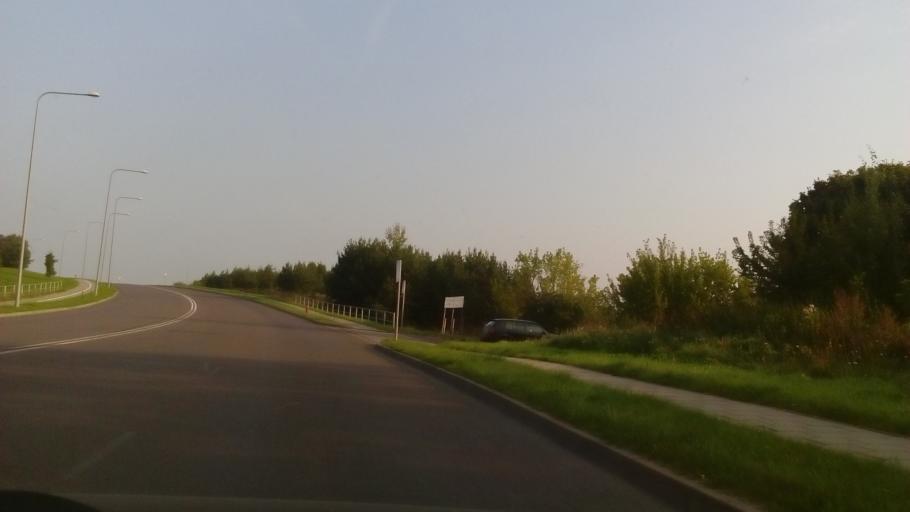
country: LT
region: Alytaus apskritis
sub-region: Alytus
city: Alytus
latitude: 54.4007
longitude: 24.0155
